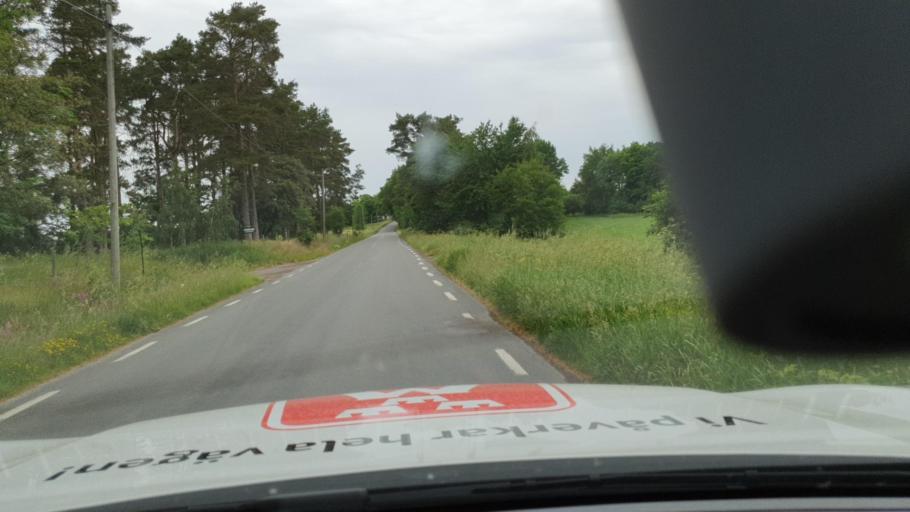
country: SE
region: Vaestra Goetaland
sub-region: Tidaholms Kommun
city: Olofstorp
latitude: 58.3084
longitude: 14.0968
